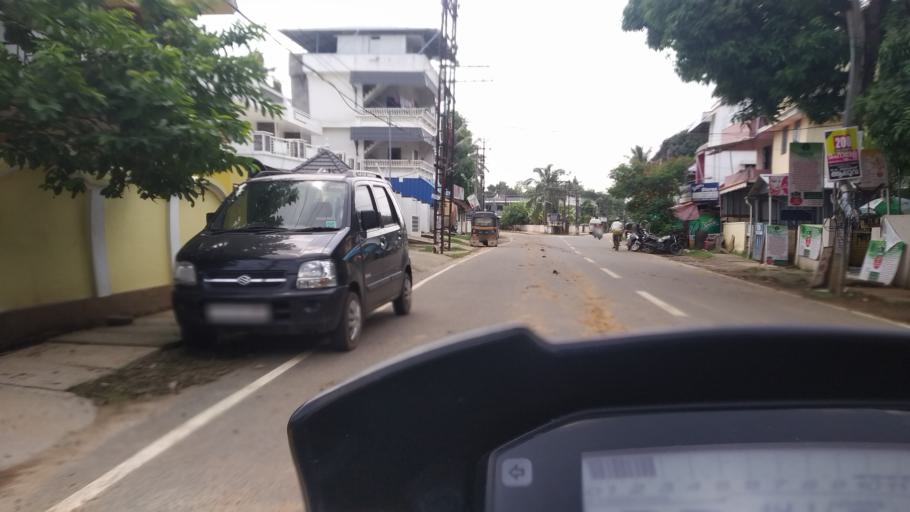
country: IN
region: Kerala
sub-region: Ernakulam
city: Aluva
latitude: 10.1168
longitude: 76.3502
